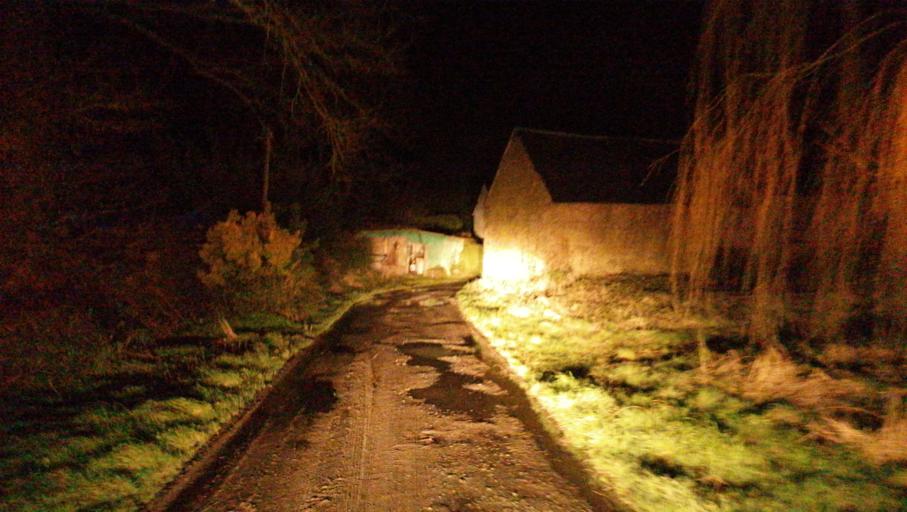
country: FR
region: Brittany
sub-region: Departement des Cotes-d'Armor
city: Saint-Agathon
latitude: 48.5812
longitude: -3.0890
